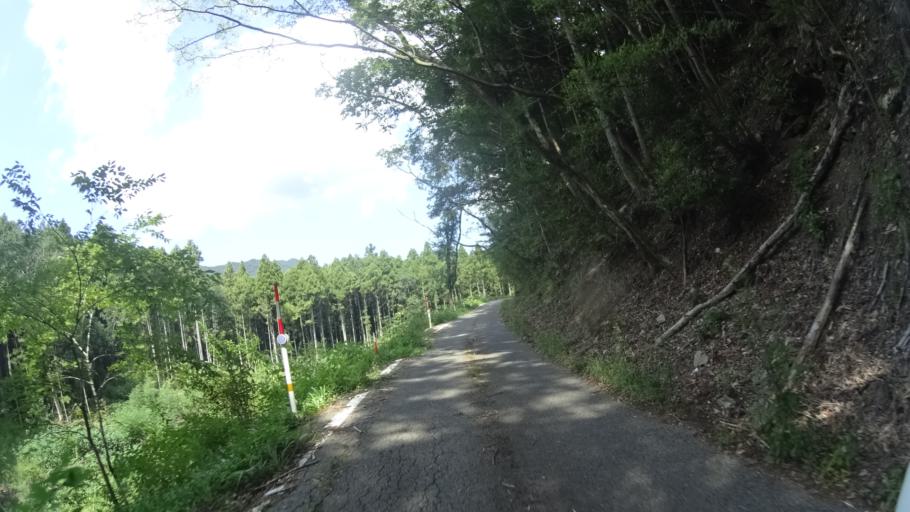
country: JP
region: Yamaguchi
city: Hagi
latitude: 34.4957
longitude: 131.5591
